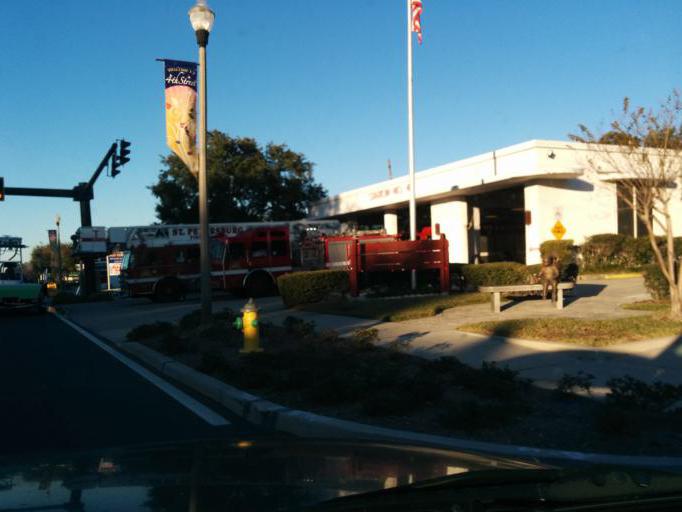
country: US
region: Florida
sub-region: Pinellas County
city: Saint Petersburg
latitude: 27.7948
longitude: -82.6385
